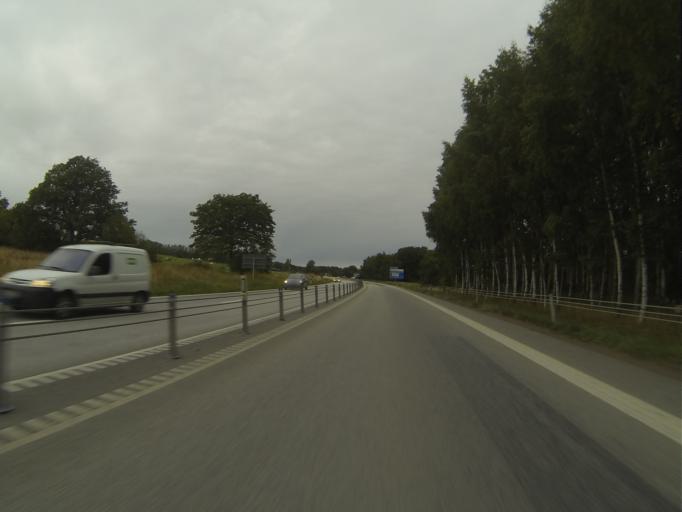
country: SE
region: Skane
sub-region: Lunds Kommun
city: Veberod
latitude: 55.6525
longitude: 13.4444
